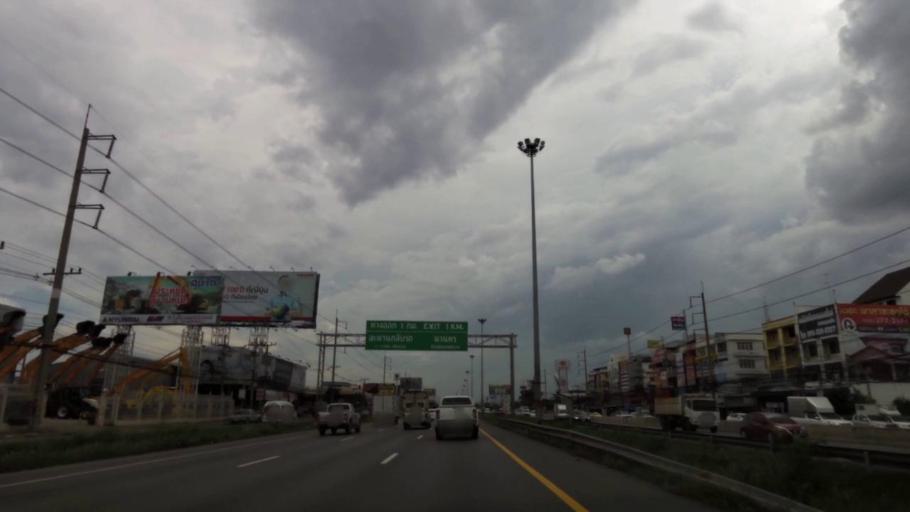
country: TH
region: Pathum Thani
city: Khlong Luang
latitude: 14.1147
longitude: 100.6187
